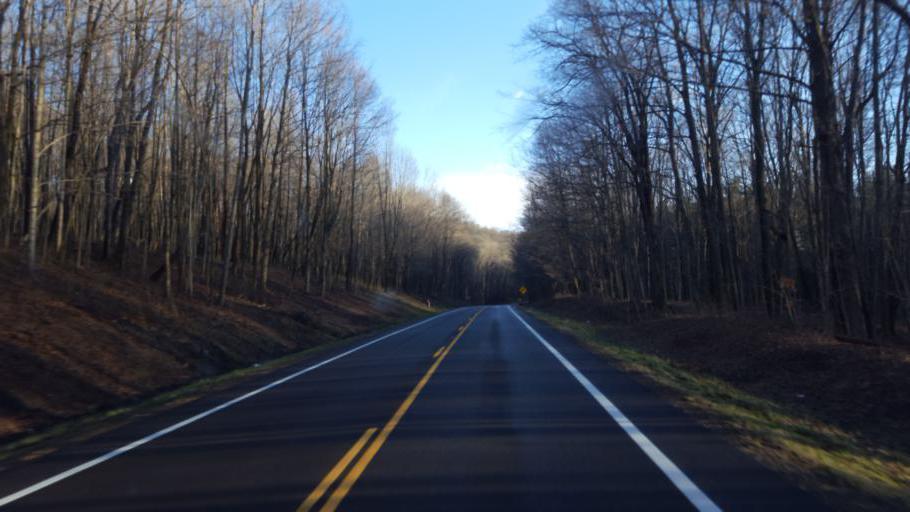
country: US
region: Ohio
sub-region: Sandusky County
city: Bellville
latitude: 40.6370
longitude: -82.3812
